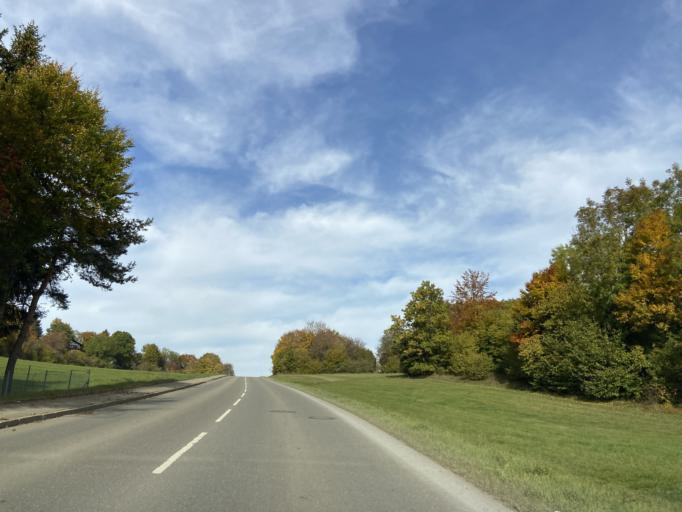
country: DE
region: Baden-Wuerttemberg
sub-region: Tuebingen Region
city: Schwenningen
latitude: 48.1019
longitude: 9.0087
